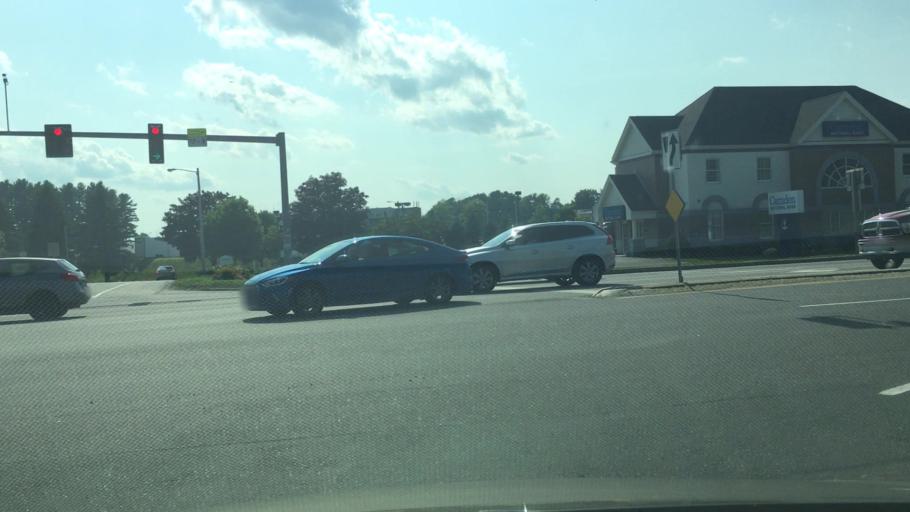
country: US
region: Maine
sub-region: Kennebec County
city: Augusta
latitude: 44.3435
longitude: -69.7928
